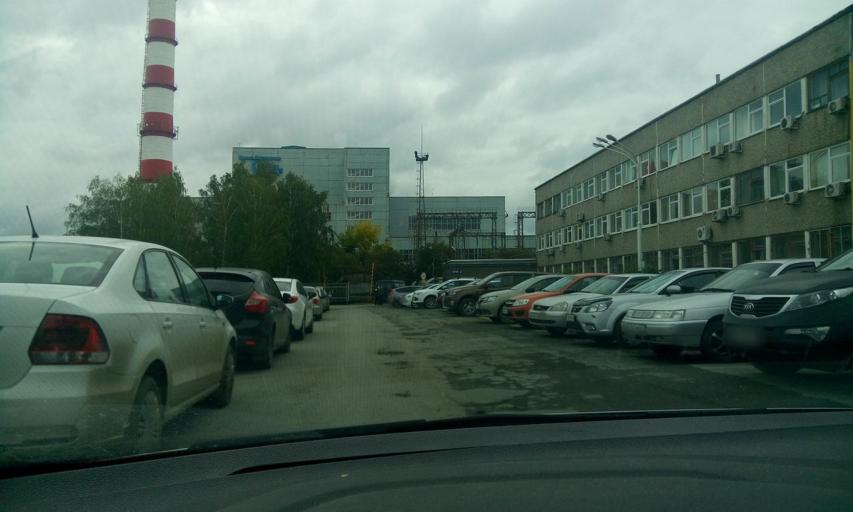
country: RU
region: Sverdlovsk
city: Yekaterinburg
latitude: 56.8514
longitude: 60.5474
